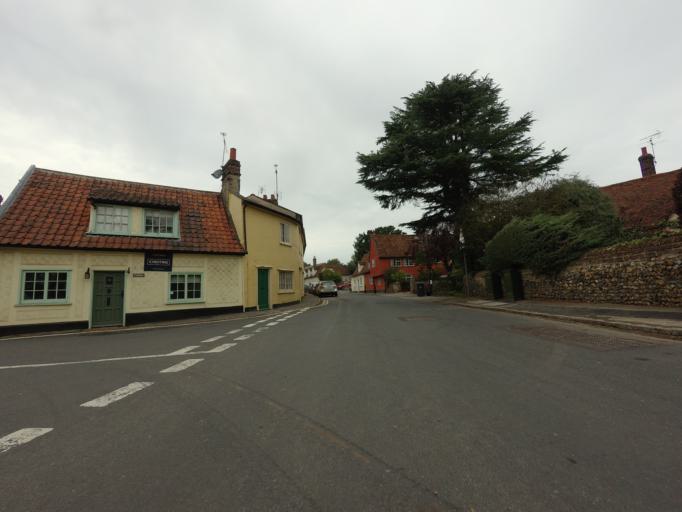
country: GB
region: England
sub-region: Essex
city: Saffron Walden
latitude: 52.0344
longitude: 0.2122
